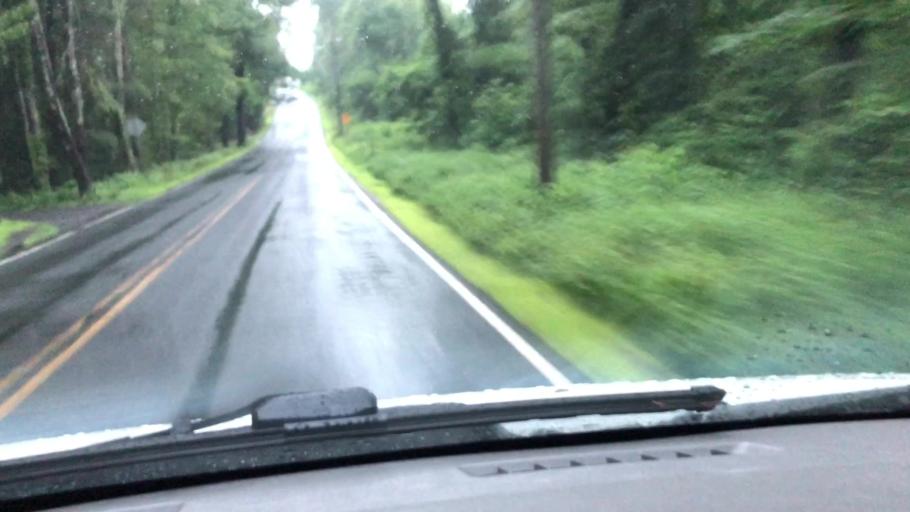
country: US
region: Massachusetts
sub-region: Hampshire County
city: Westhampton
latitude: 42.2843
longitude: -72.7581
